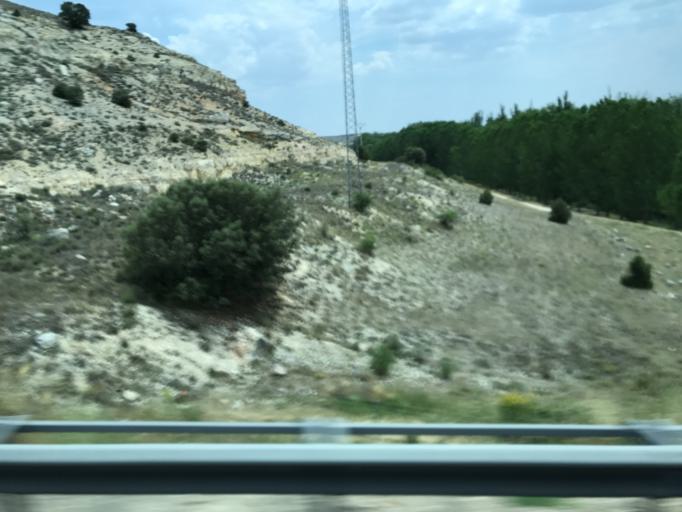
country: ES
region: Castille and Leon
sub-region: Provincia de Burgos
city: Milagros
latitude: 41.5818
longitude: -3.7059
